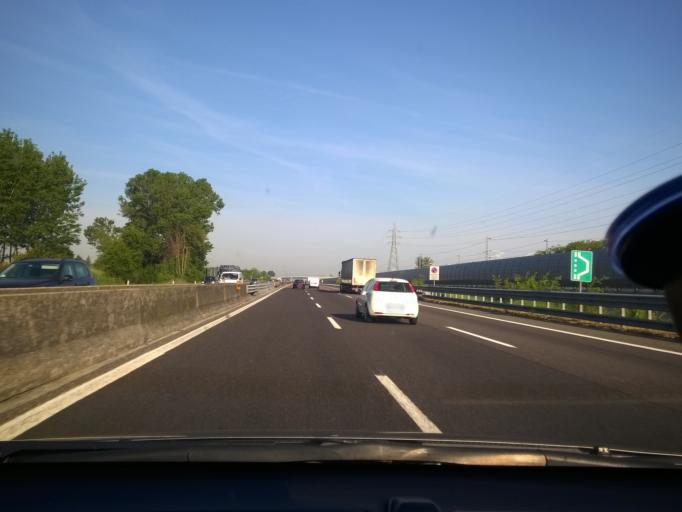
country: IT
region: Emilia-Romagna
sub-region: Provincia di Modena
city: Campogalliano
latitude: 44.6800
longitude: 10.8090
